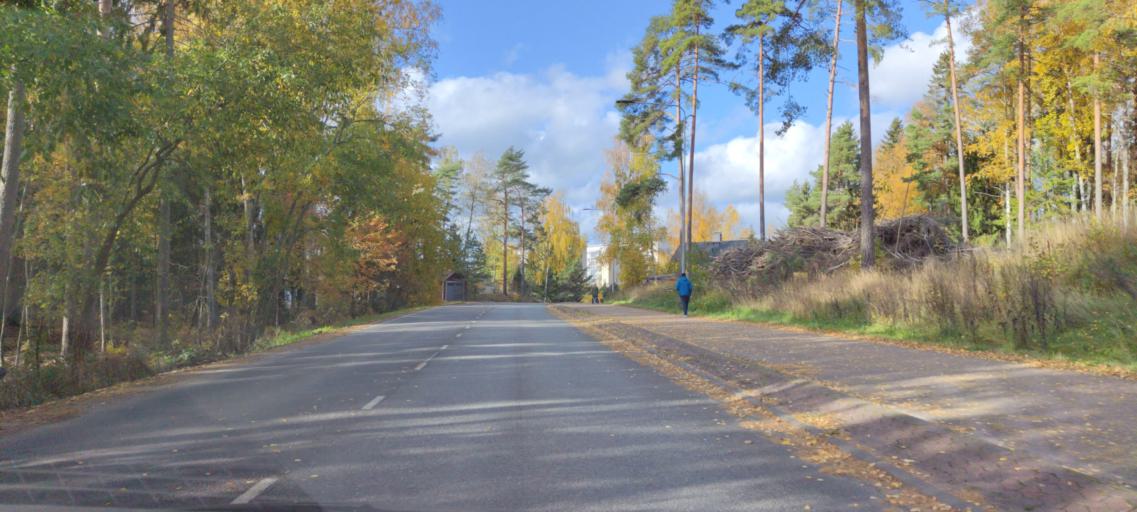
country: FI
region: Varsinais-Suomi
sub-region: Turku
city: Kaarina
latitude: 60.4075
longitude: 22.3182
